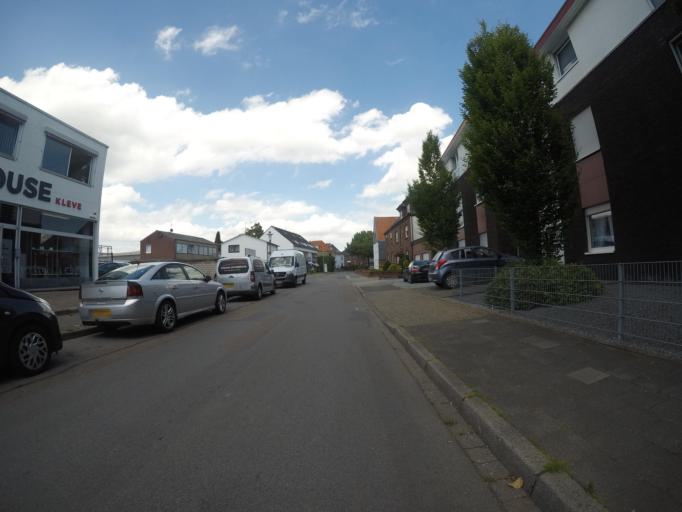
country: DE
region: North Rhine-Westphalia
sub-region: Regierungsbezirk Dusseldorf
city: Kleve
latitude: 51.7758
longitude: 6.1263
